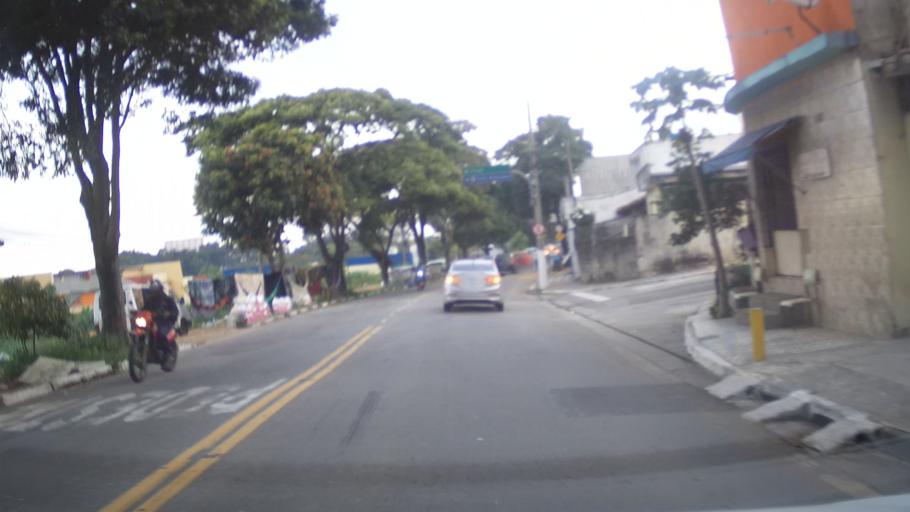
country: BR
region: Sao Paulo
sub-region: Guarulhos
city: Guarulhos
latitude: -23.4535
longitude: -46.5027
